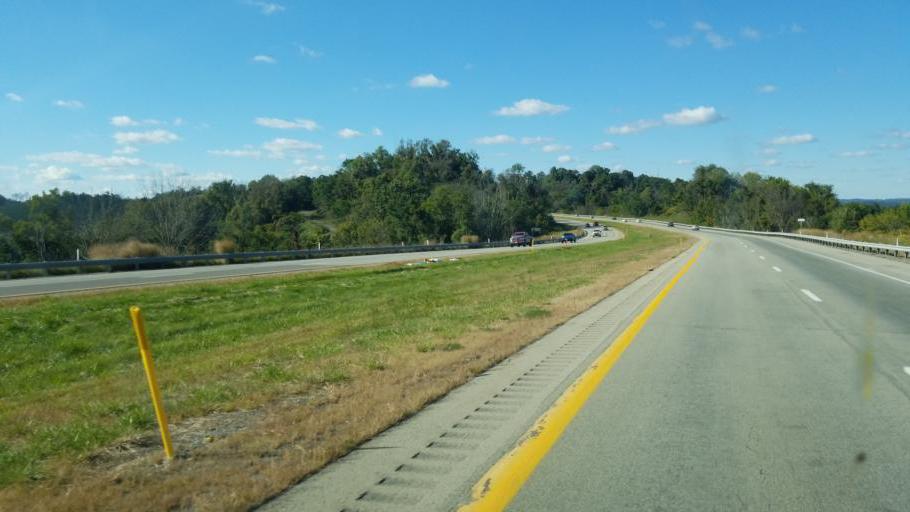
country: US
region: Pennsylvania
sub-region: Greene County
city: Morrisville
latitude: 39.8625
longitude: -80.1242
